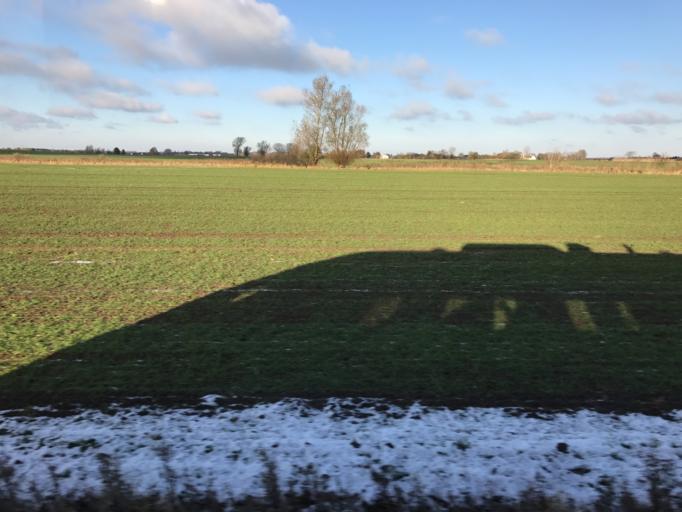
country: DK
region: Zealand
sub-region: Stevns Kommune
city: Harlev
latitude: 55.3520
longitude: 12.2874
